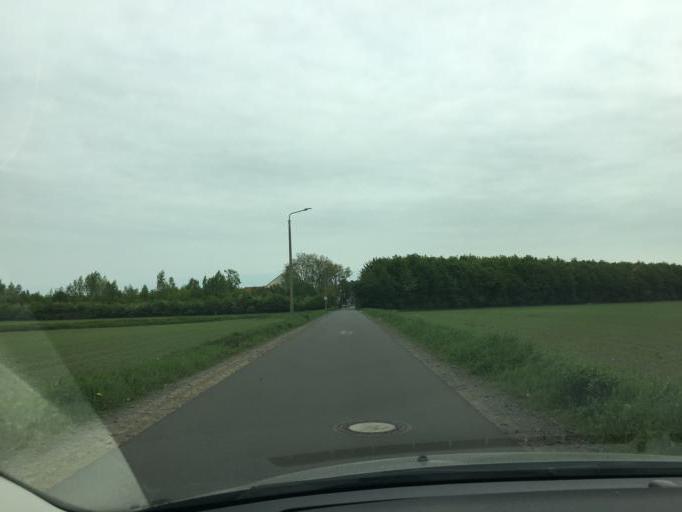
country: DE
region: Saxony
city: Taucha
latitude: 51.3696
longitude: 12.4463
